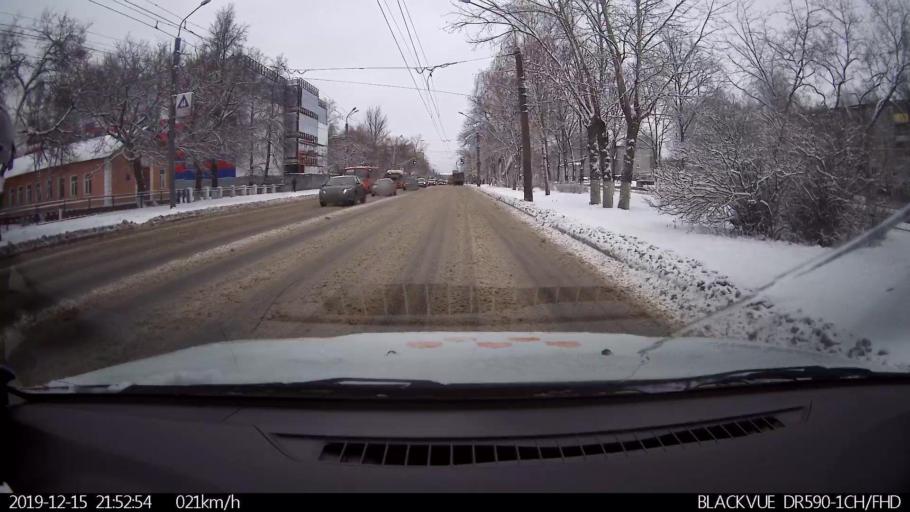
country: RU
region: Nizjnij Novgorod
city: Burevestnik
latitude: 56.2294
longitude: 43.8699
